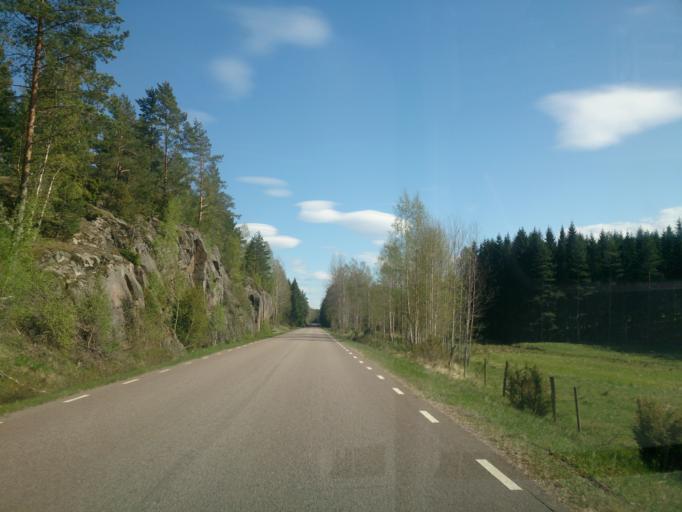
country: SE
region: OEstergoetland
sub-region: Linkopings Kommun
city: Ljungsbro
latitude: 58.6050
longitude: 15.4827
